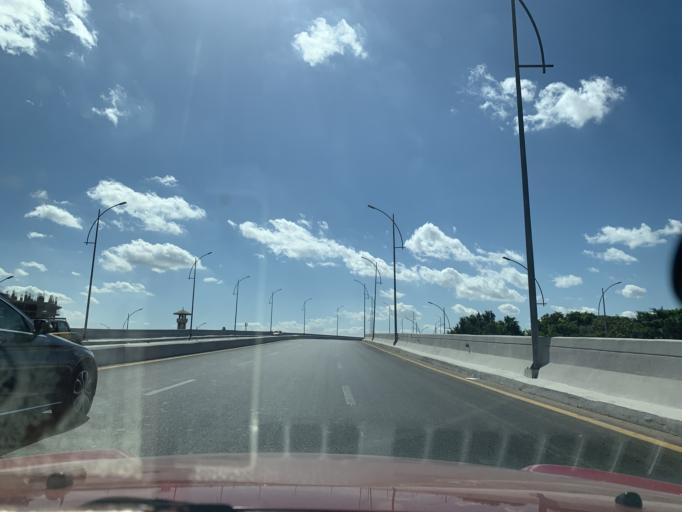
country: EG
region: Alexandria
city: Alexandria
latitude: 31.2017
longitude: 29.9534
